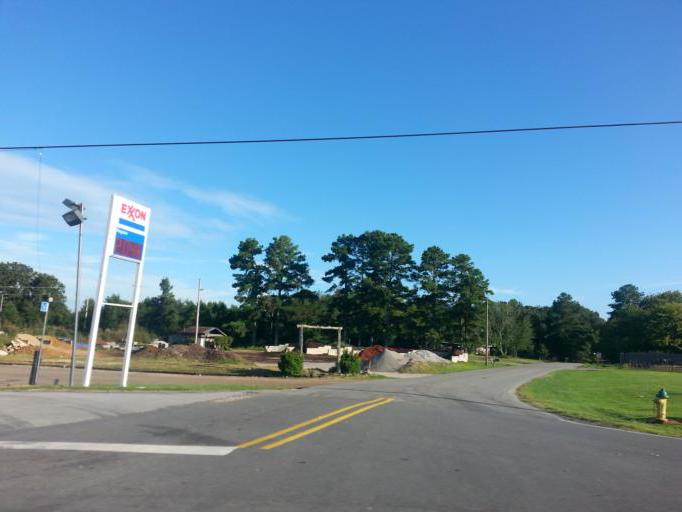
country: US
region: Alabama
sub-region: Lauderdale County
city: East Florence
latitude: 34.8383
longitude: -87.6016
